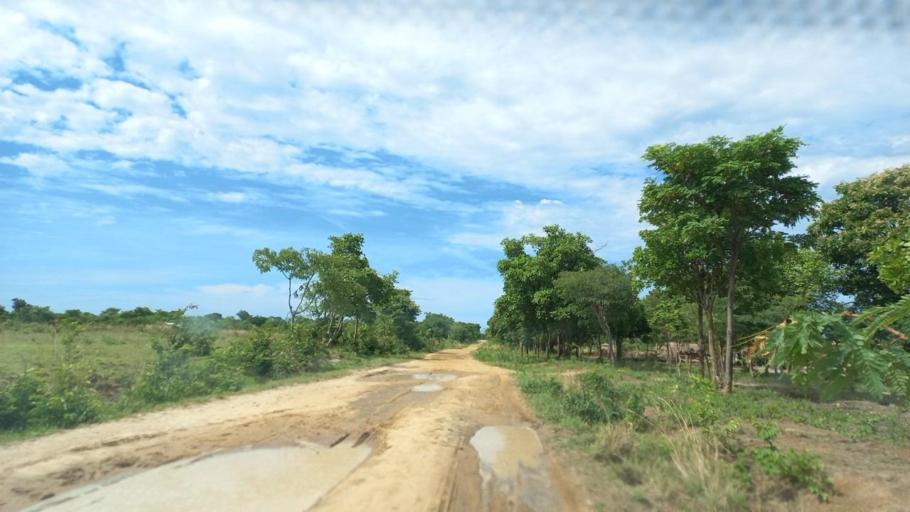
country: ZM
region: North-Western
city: Kabompo
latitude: -13.5182
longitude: 24.3869
